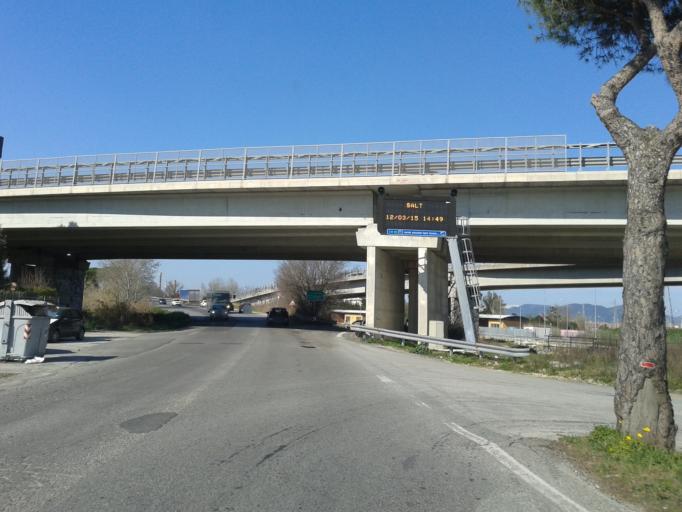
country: IT
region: Tuscany
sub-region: Province of Pisa
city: Pisa
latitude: 43.6993
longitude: 10.3891
